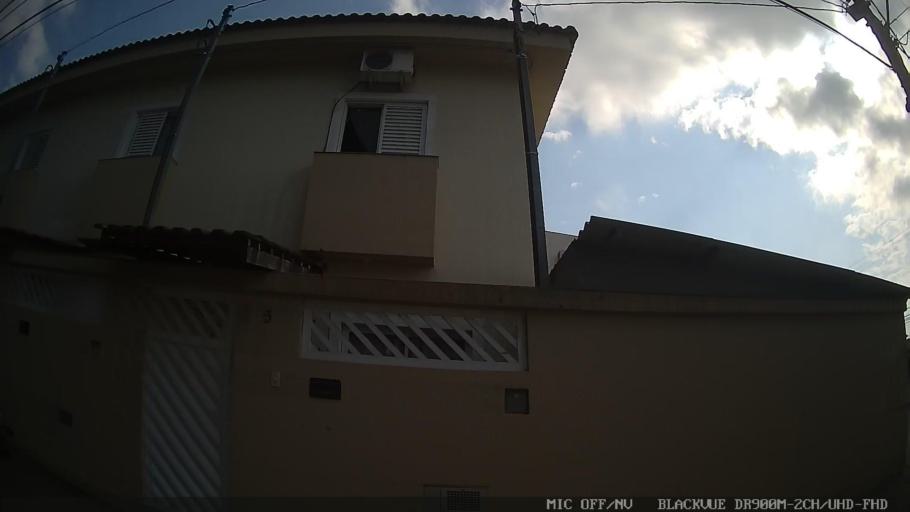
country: BR
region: Sao Paulo
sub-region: Santos
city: Santos
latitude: -23.9545
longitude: -46.2869
